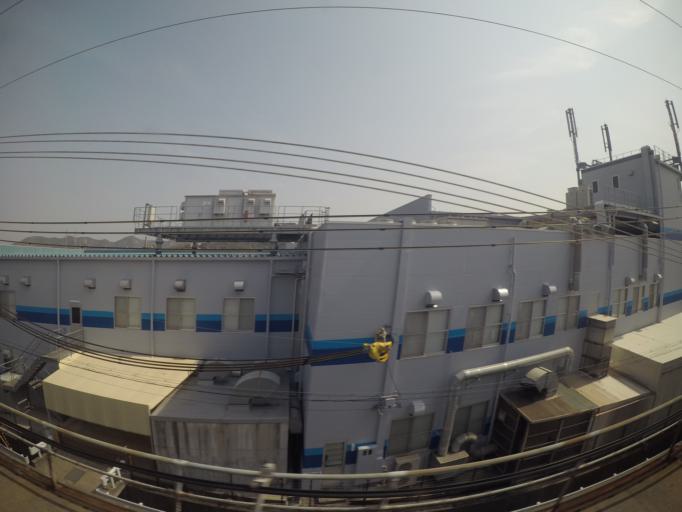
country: JP
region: Hyogo
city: Shirahamacho-usazakiminami
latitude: 34.8043
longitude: 134.7517
